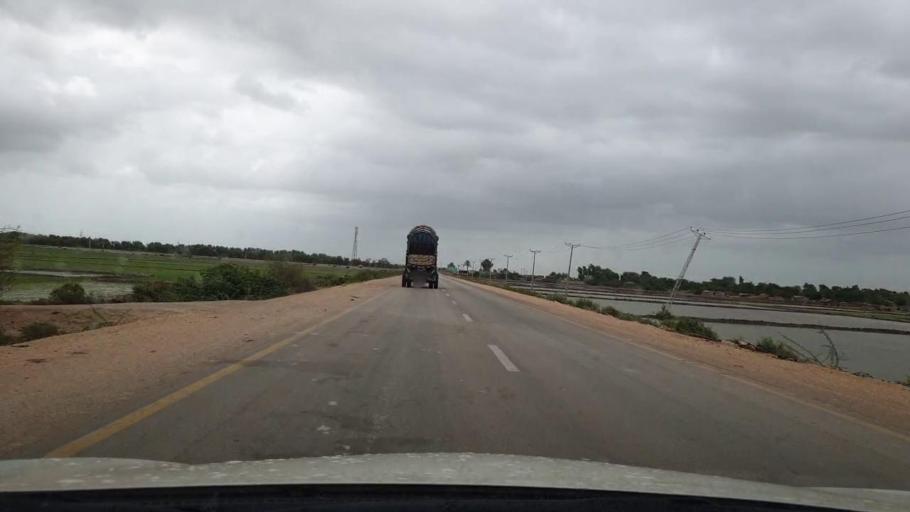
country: PK
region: Sindh
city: Badin
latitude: 24.6556
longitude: 68.7235
